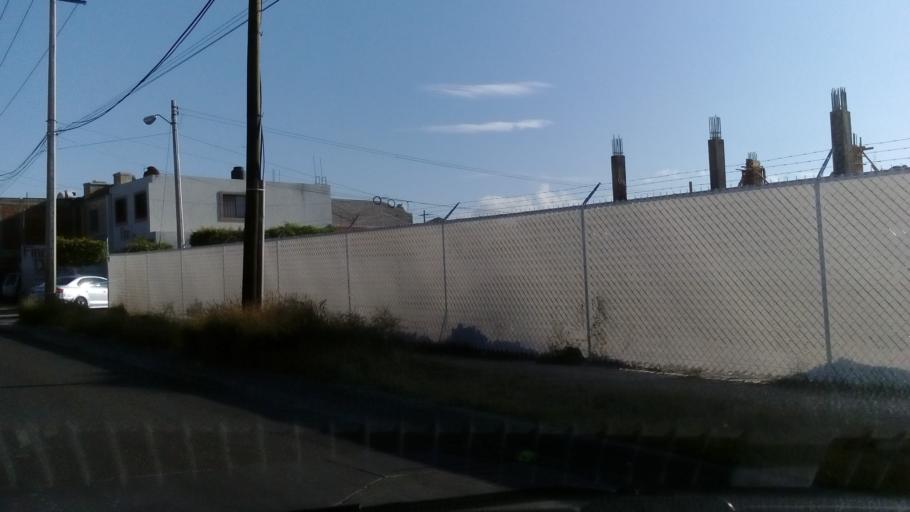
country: MX
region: Guanajuato
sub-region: Leon
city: Ejido la Joya
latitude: 21.1120
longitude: -101.7108
